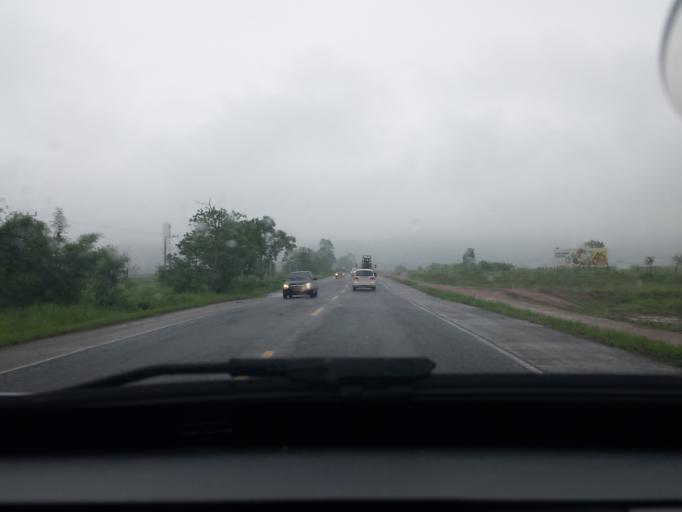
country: BR
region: Santa Catarina
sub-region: Itajai
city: Itajai
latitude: -26.8342
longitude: -48.7465
